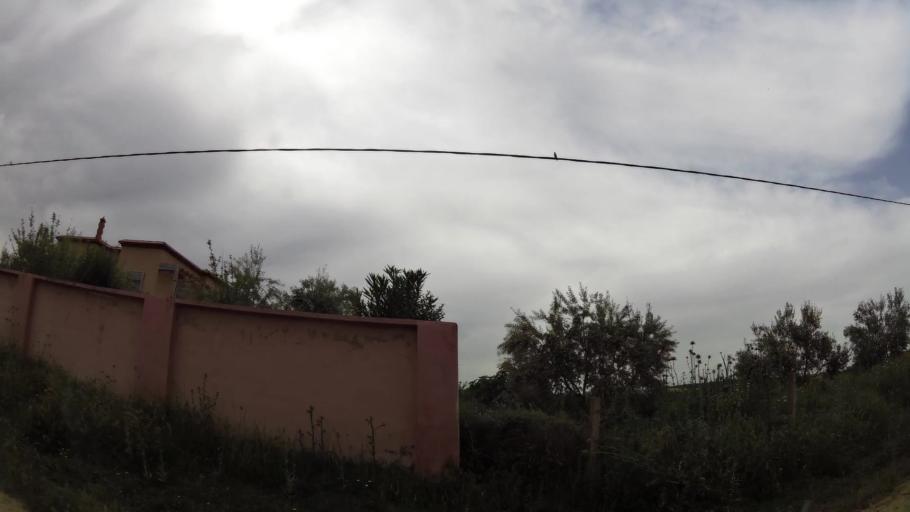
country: MA
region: Rabat-Sale-Zemmour-Zaer
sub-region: Khemisset
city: Khemisset
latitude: 33.7504
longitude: -6.2013
